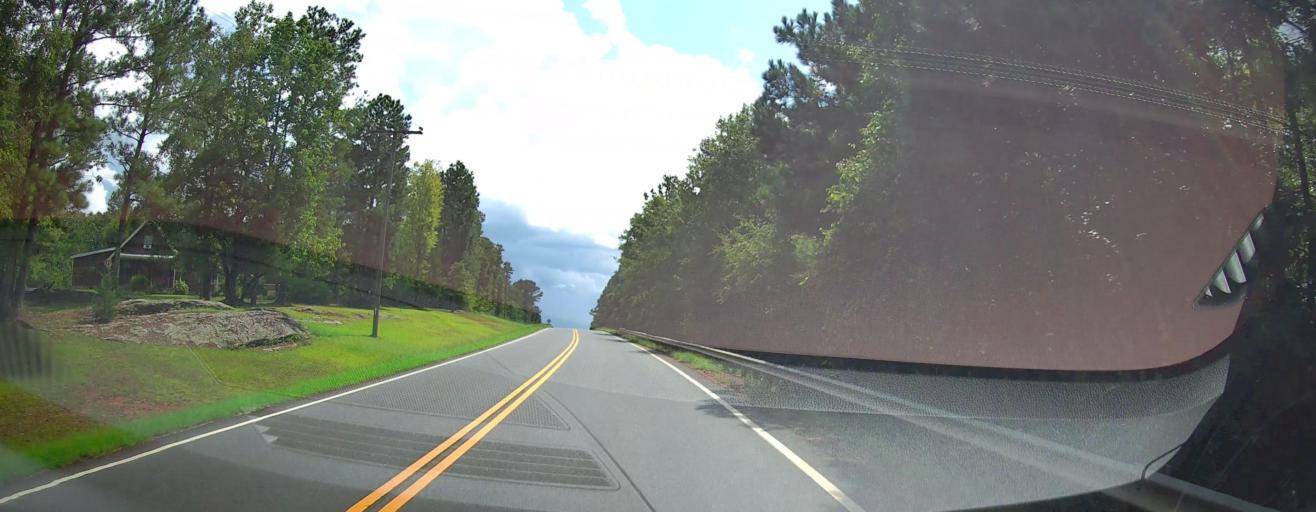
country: US
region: Georgia
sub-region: Monroe County
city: Forsyth
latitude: 32.8831
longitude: -83.9721
